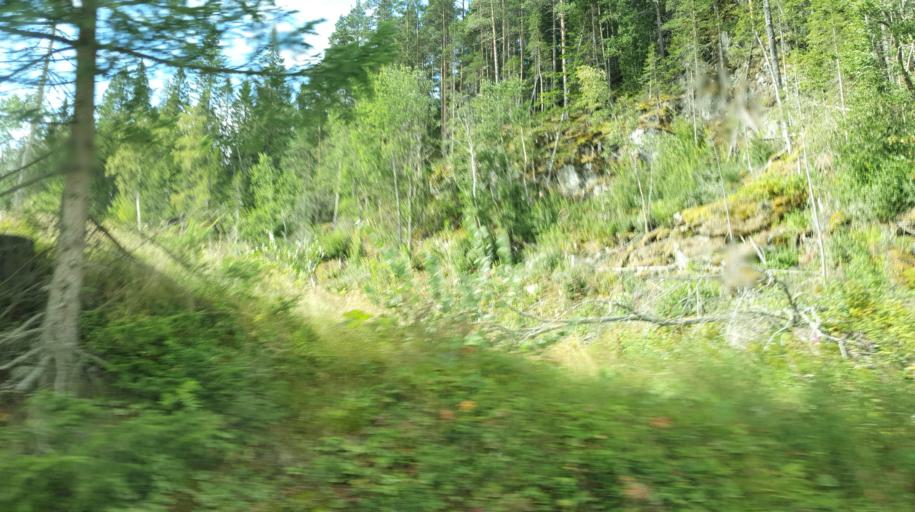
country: NO
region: Nord-Trondelag
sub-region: Levanger
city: Skogn
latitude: 63.5967
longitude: 11.2681
